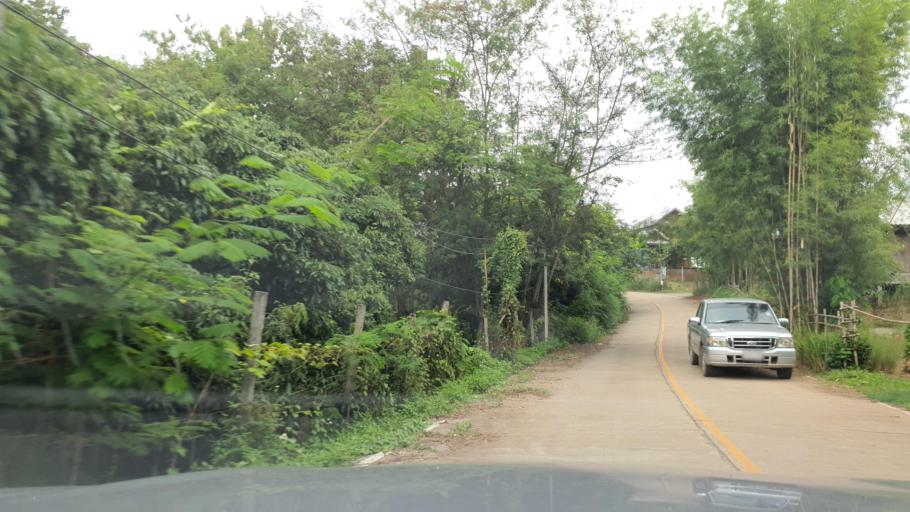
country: TH
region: Chiang Mai
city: San Sai
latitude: 18.9353
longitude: 98.9064
